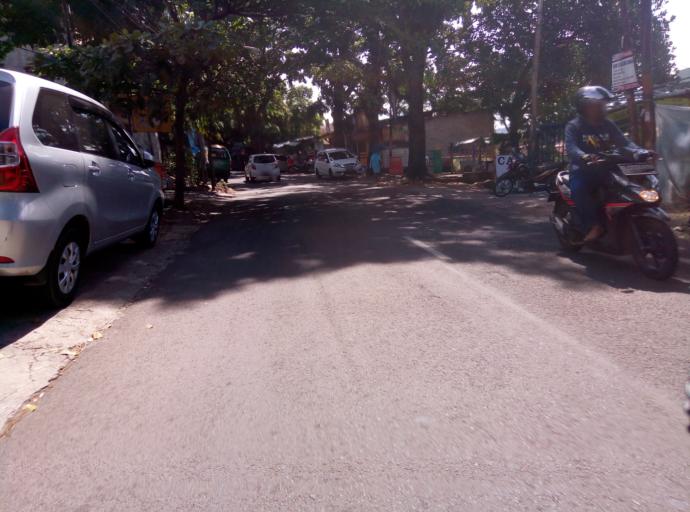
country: ID
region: West Java
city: Bandung
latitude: -6.8893
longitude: 107.6262
